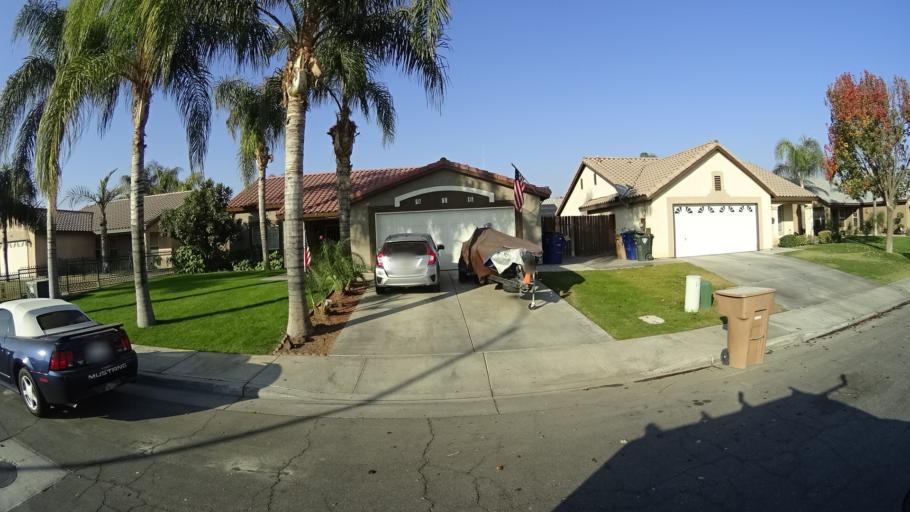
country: US
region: California
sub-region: Kern County
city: Greenfield
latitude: 35.2848
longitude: -119.0129
